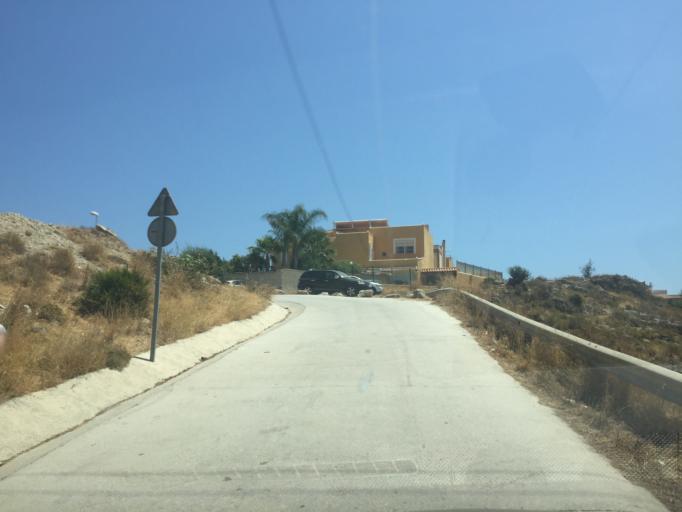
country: ES
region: Andalusia
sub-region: Provincia de Malaga
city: Nerja
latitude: 36.7643
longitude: -3.8746
